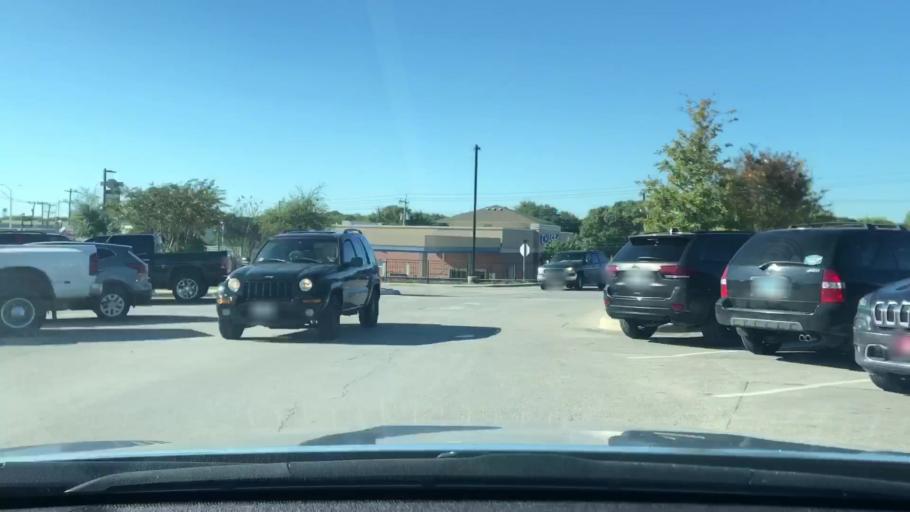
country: US
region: Texas
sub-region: Bexar County
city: Universal City
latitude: 29.5467
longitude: -98.3129
